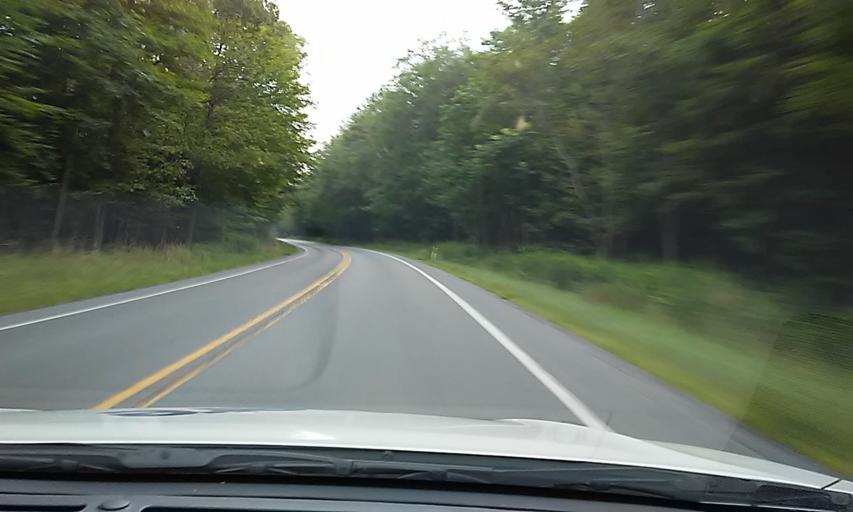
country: US
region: Pennsylvania
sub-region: McKean County
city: Kane
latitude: 41.6072
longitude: -78.8413
